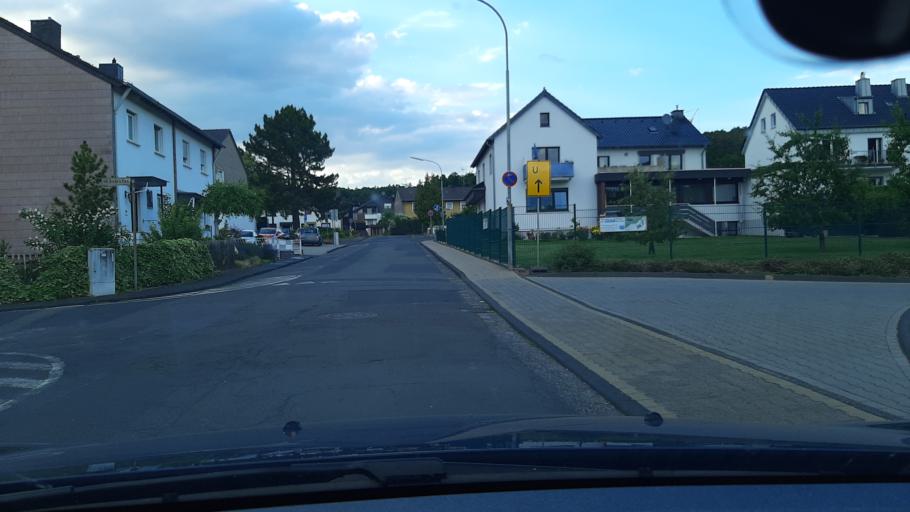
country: DE
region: North Rhine-Westphalia
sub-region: Regierungsbezirk Koln
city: Mechernich
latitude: 50.5931
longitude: 6.6493
